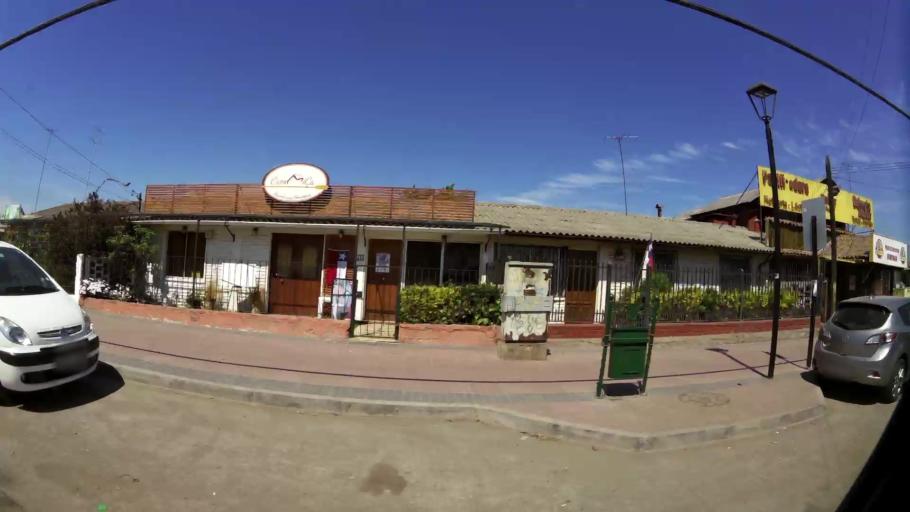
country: CL
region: Santiago Metropolitan
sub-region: Provincia de Talagante
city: Talagante
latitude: -33.6608
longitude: -70.9209
